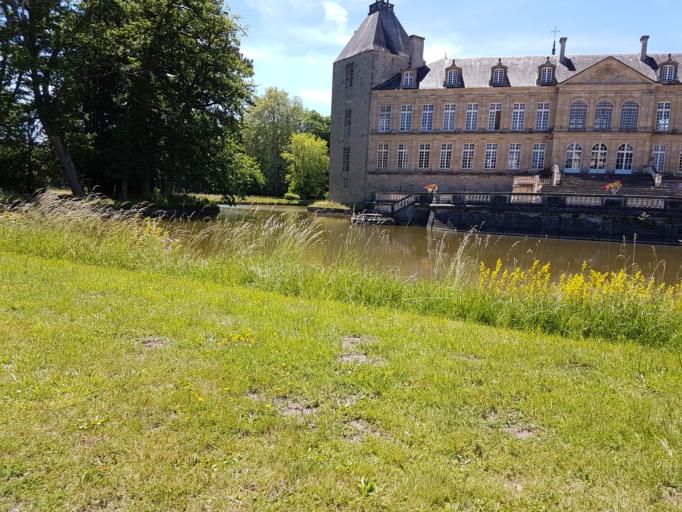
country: FR
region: Bourgogne
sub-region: Departement de Saone-et-Loire
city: Epinac
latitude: 47.0117
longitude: 4.4736
